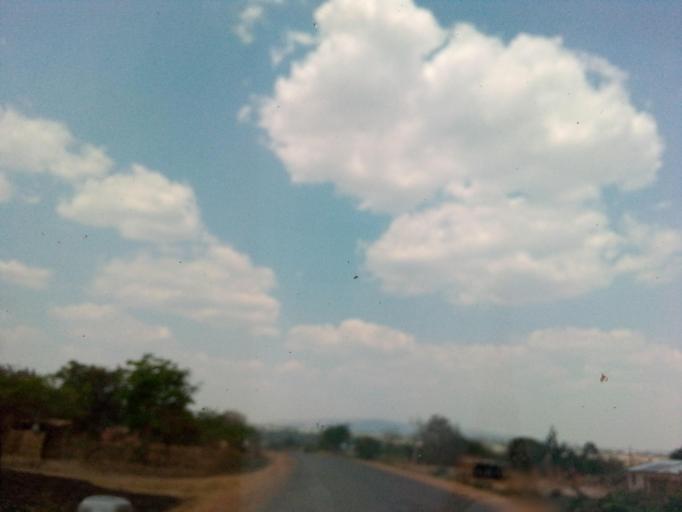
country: ZM
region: Northern
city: Mpika
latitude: -11.8362
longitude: 31.3859
